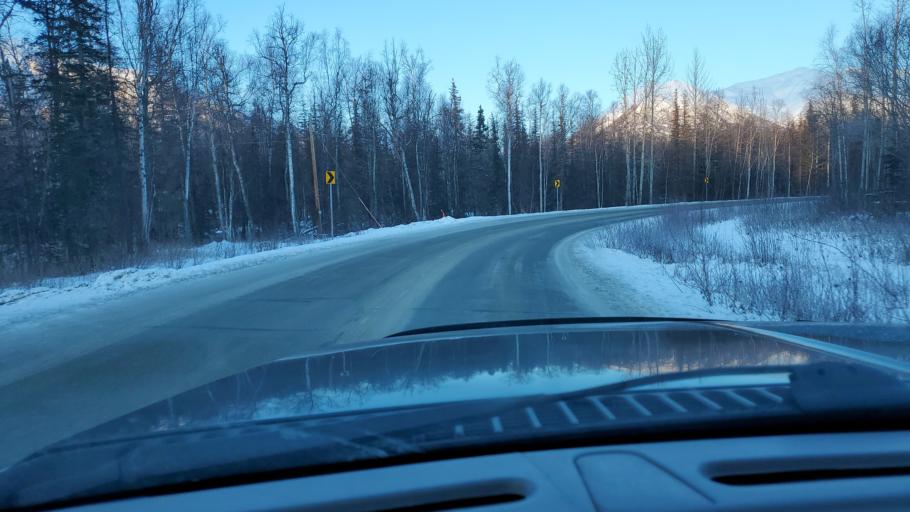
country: US
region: Alaska
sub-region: Matanuska-Susitna Borough
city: Fishhook
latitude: 61.6866
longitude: -149.2465
